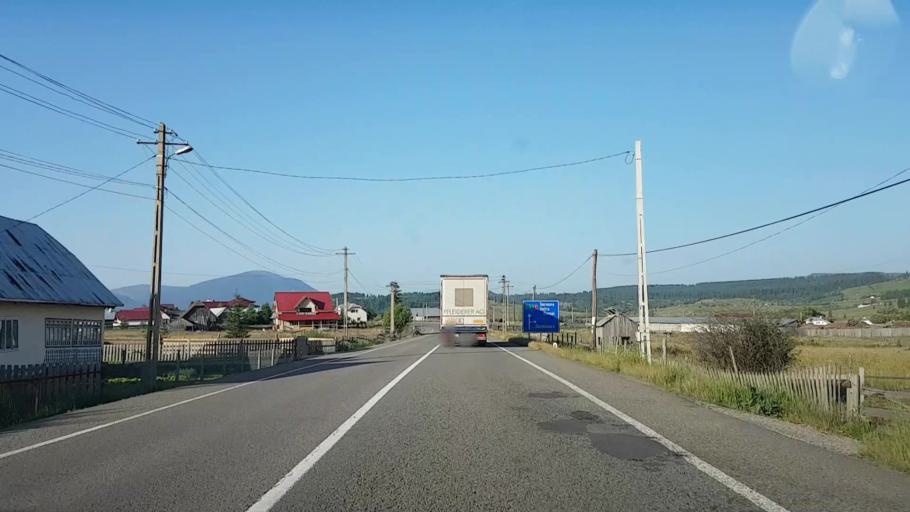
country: RO
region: Suceava
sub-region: Comuna Poiana Stampei
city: Poiana Stampei
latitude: 47.3082
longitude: 25.1245
